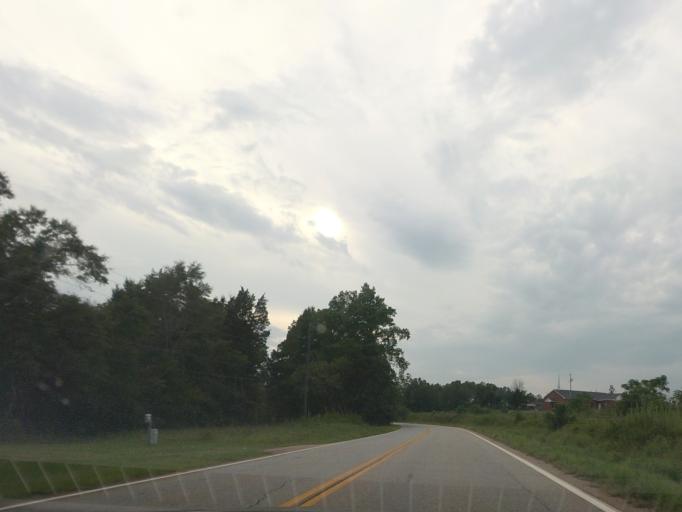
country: US
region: Georgia
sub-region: Twiggs County
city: Jeffersonville
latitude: 32.7185
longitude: -83.3996
